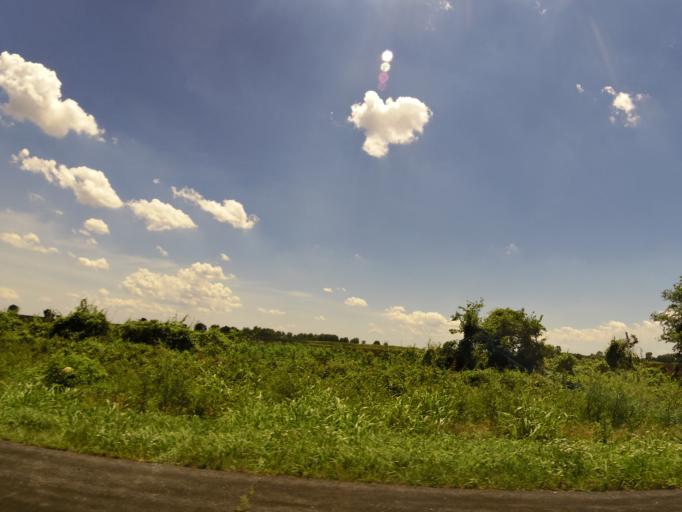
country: US
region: Missouri
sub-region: Pemiscot County
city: Hayti
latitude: 36.1935
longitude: -89.7180
